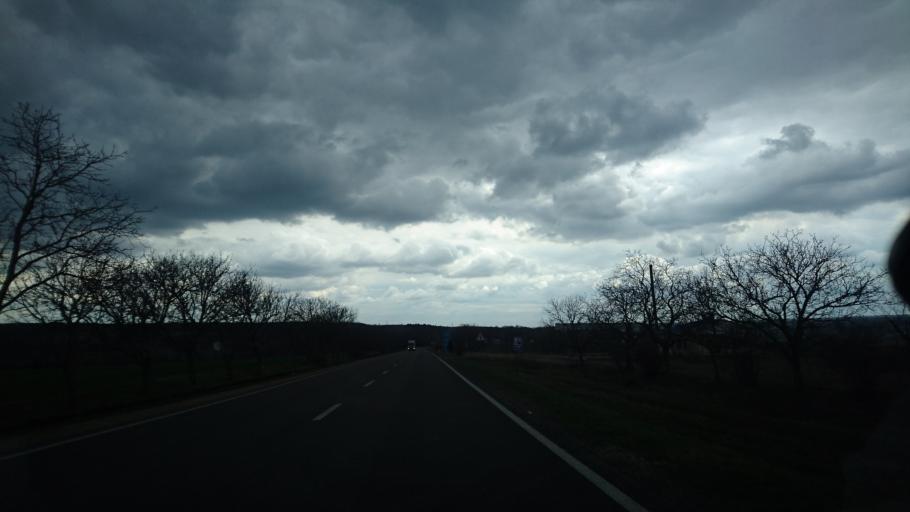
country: MD
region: Gagauzia
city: Bugeac
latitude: 46.3698
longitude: 28.6813
